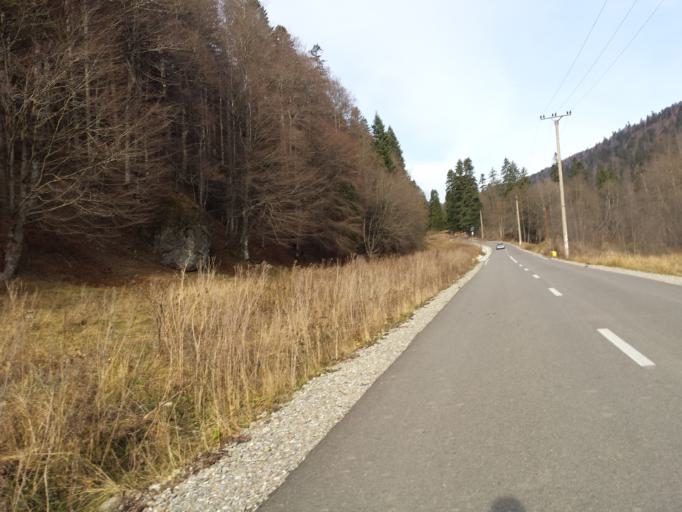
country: RO
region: Prahova
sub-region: Oras Azuga
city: Azuga
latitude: 45.4330
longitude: 25.5305
